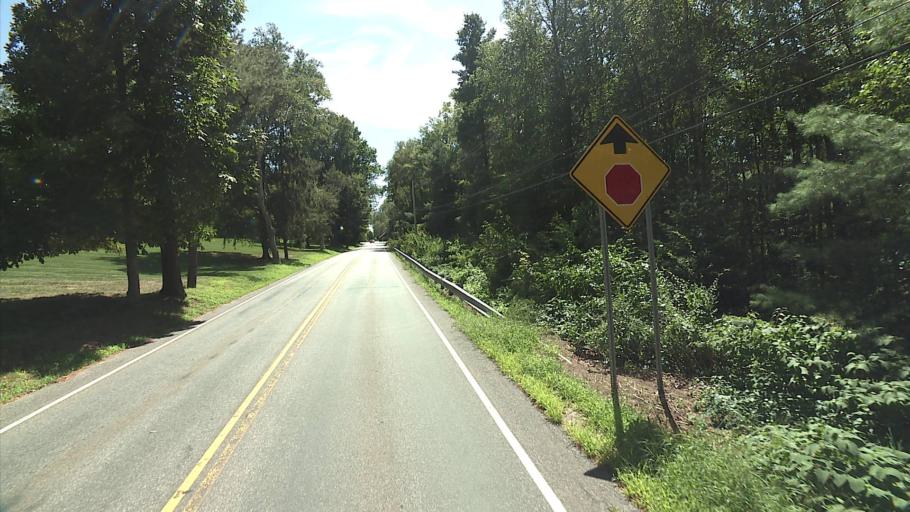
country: US
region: Connecticut
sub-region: Windham County
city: South Woodstock
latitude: 41.8770
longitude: -71.9752
